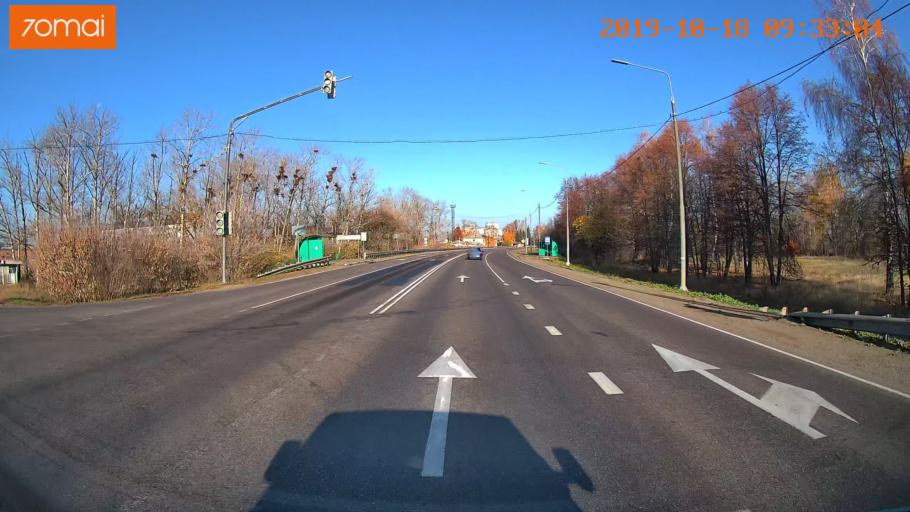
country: RU
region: Tula
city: Yefremov
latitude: 53.1631
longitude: 38.1532
